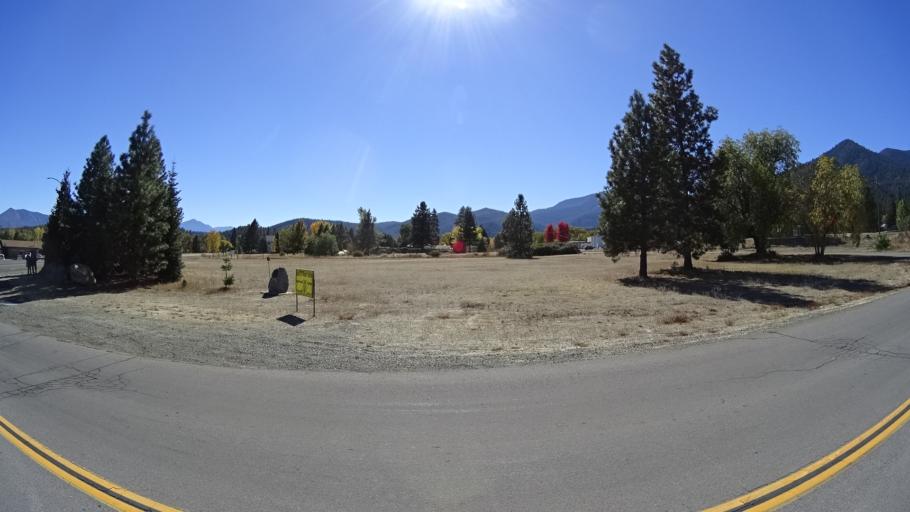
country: US
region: California
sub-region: Siskiyou County
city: Yreka
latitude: 41.4632
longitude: -122.8972
